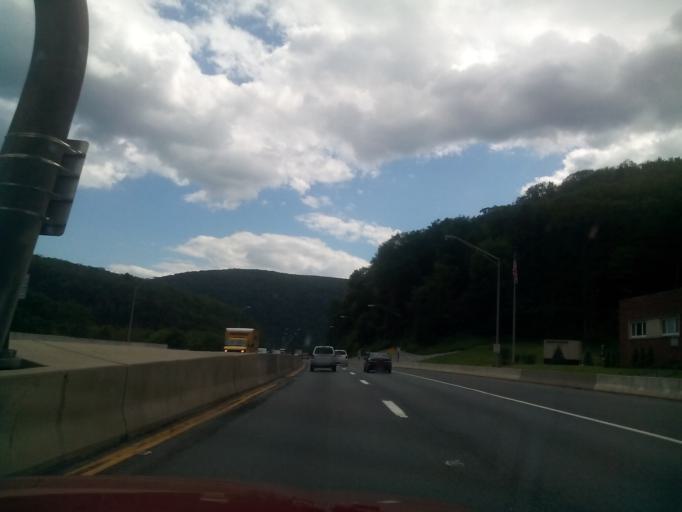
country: US
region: Pennsylvania
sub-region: Monroe County
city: East Stroudsburg
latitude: 40.9832
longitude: -75.1379
